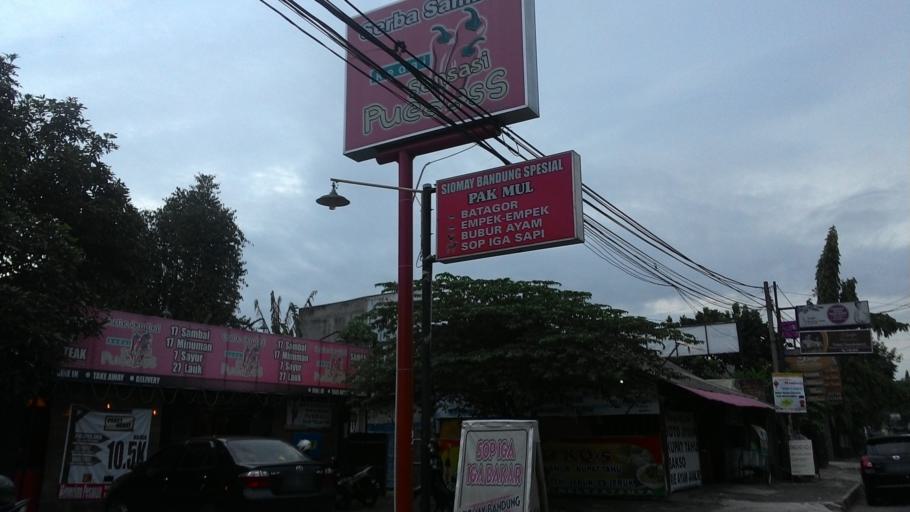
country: ID
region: Daerah Istimewa Yogyakarta
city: Yogyakarta
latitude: -7.7923
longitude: 110.3908
